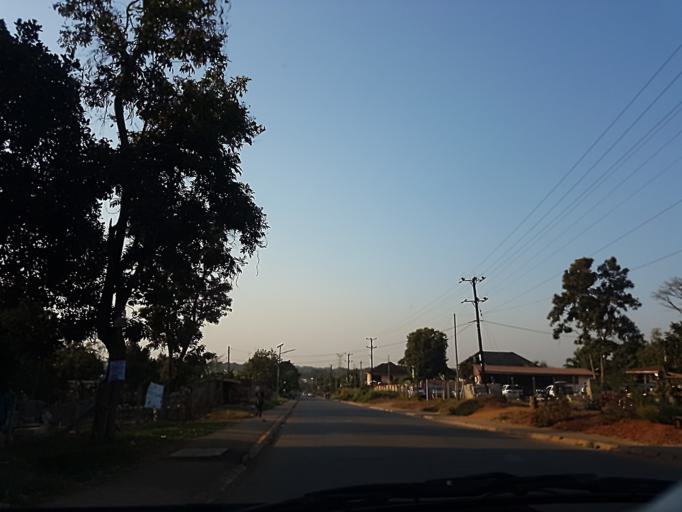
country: UG
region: Central Region
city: Kampala Central Division
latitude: 0.3982
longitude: 32.5924
